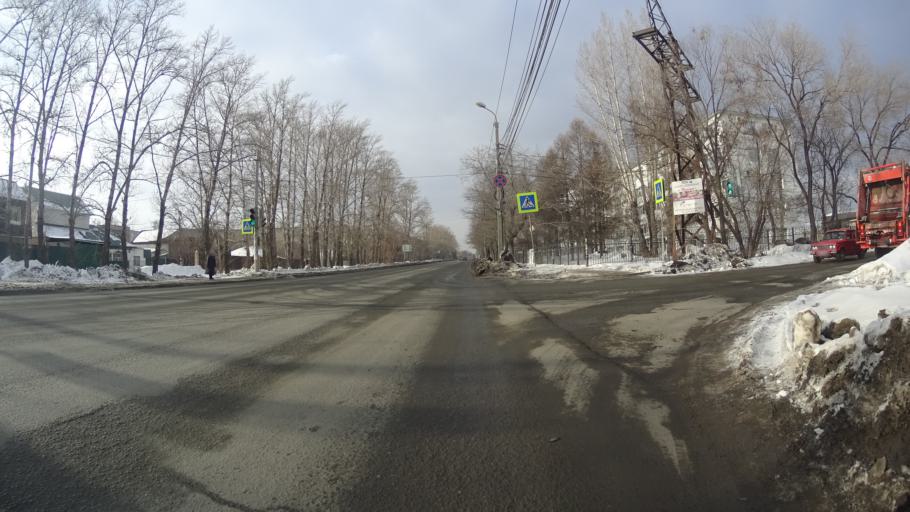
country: RU
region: Chelyabinsk
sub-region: Gorod Chelyabinsk
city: Chelyabinsk
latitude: 55.1240
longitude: 61.3730
